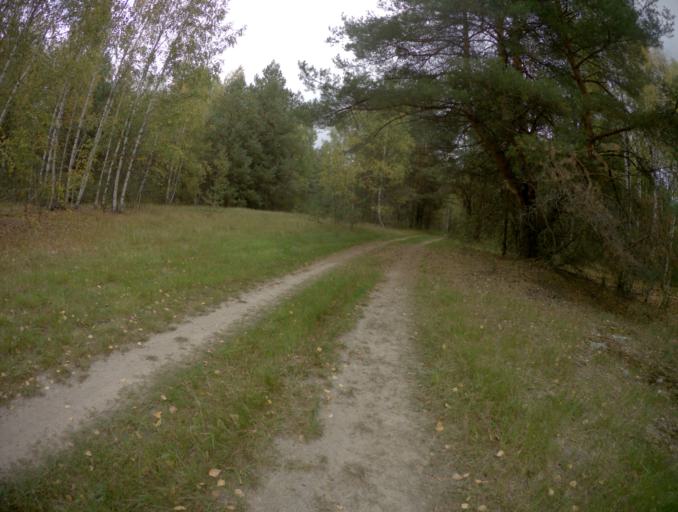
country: RU
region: Vladimir
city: Urshel'skiy
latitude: 55.7768
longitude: 40.1493
